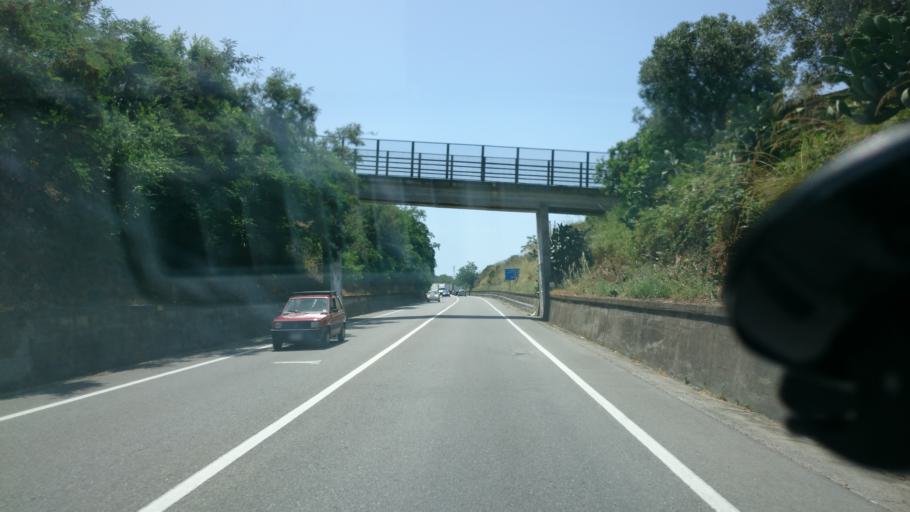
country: IT
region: Calabria
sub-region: Provincia di Cosenza
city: Cittadella del Capo
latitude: 39.5653
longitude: 15.8751
